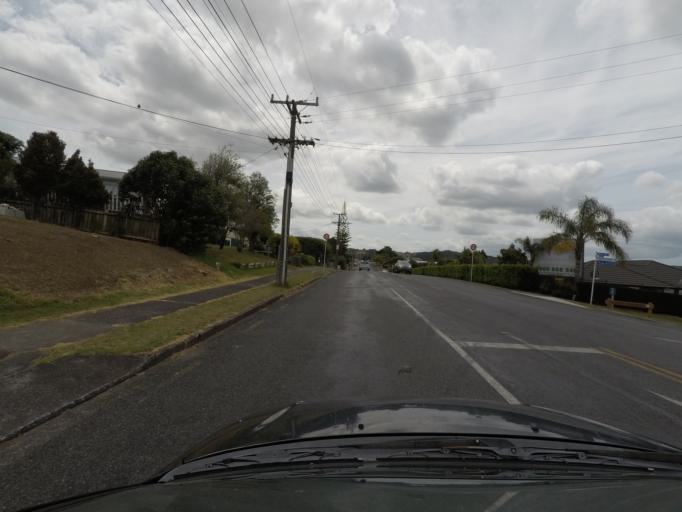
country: NZ
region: Northland
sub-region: Whangarei
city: Whangarei
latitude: -35.6830
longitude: 174.3267
